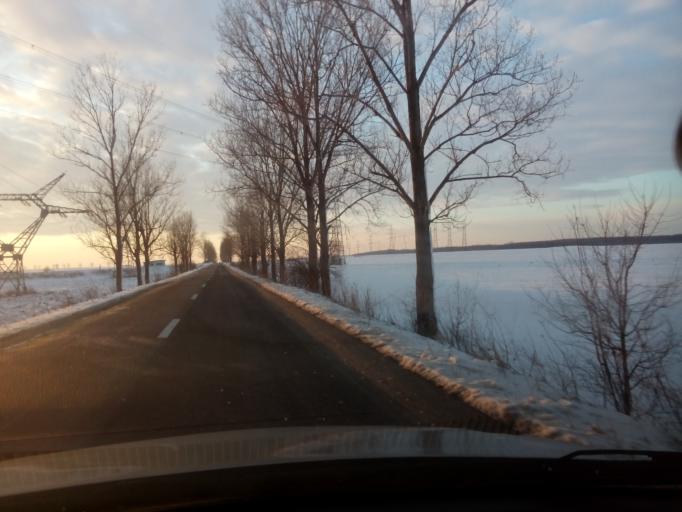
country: RO
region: Calarasi
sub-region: Comuna Luica
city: Luica
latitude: 44.2251
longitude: 26.5673
